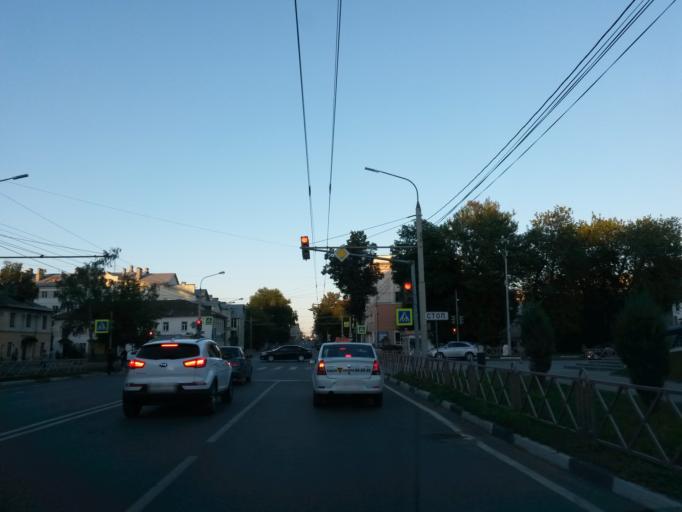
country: RU
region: Jaroslavl
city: Yaroslavl
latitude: 57.6216
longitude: 39.8699
